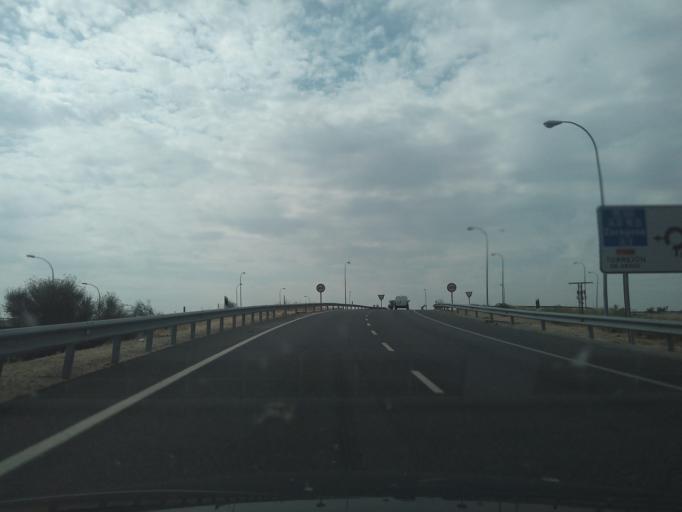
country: ES
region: Madrid
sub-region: Provincia de Madrid
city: San Fernando de Henares
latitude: 40.4357
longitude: -3.5076
